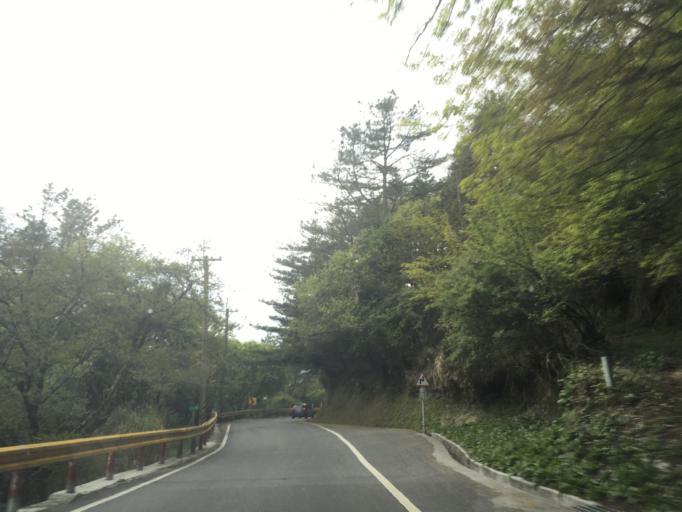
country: TW
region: Taiwan
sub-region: Hualien
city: Hualian
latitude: 24.1802
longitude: 121.3143
